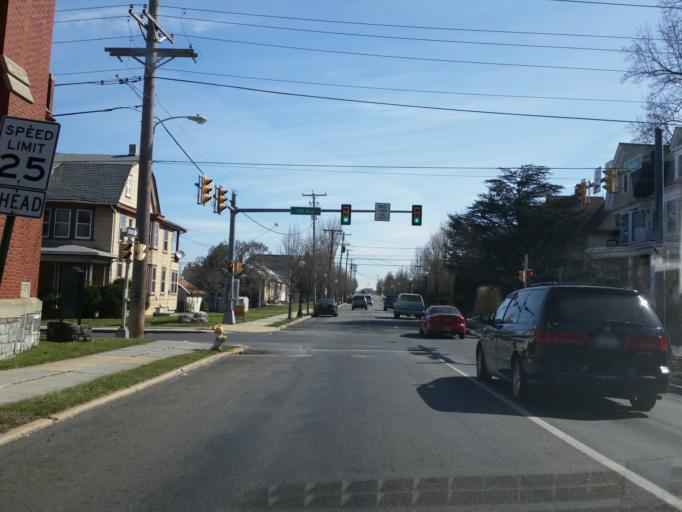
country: US
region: Pennsylvania
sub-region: Lebanon County
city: Hebron
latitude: 40.3385
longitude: -76.4040
